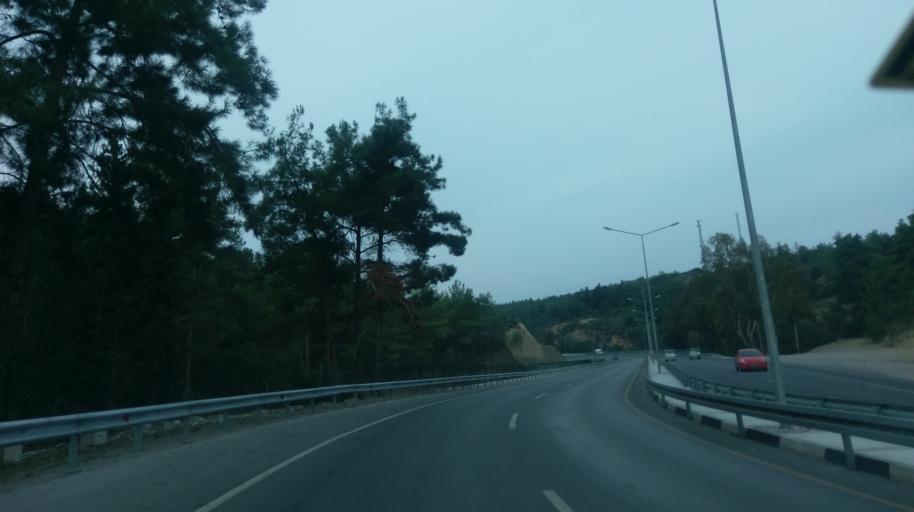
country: CY
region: Keryneia
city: Kyrenia
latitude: 35.3070
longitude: 33.3207
